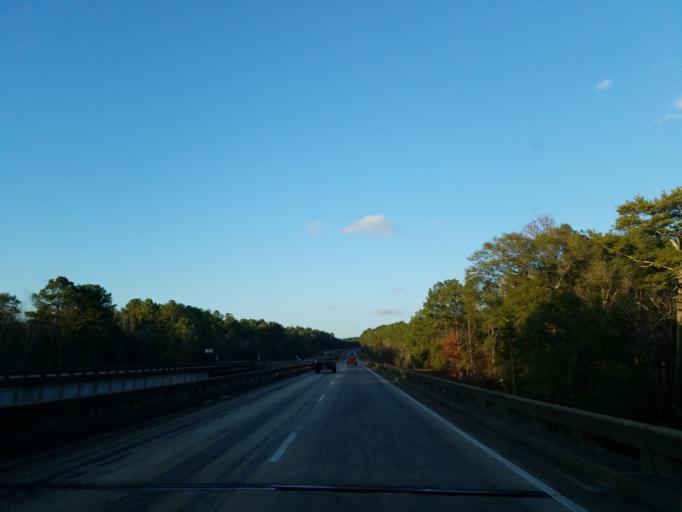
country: US
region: Mississippi
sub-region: Clarke County
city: Stonewall
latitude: 32.2264
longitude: -88.8326
